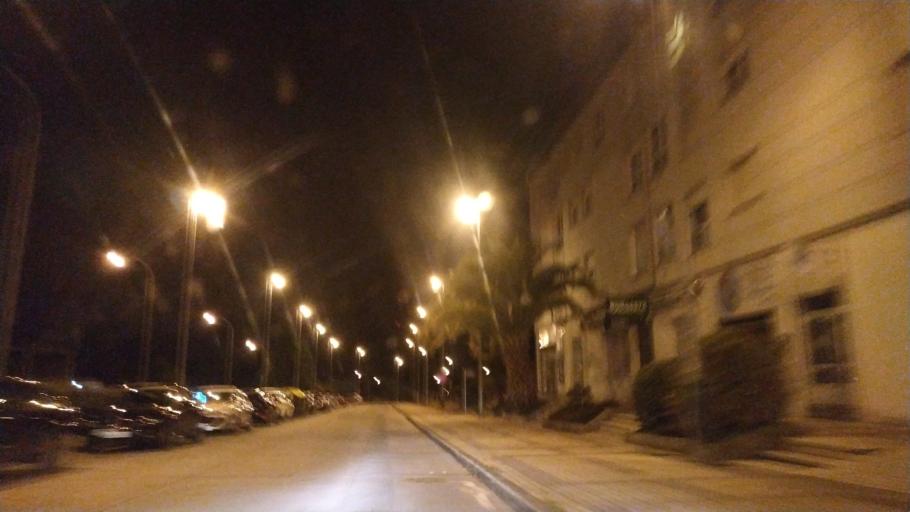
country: ES
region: Galicia
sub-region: Provincia de Lugo
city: Lugo
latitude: 42.9940
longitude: -7.5499
